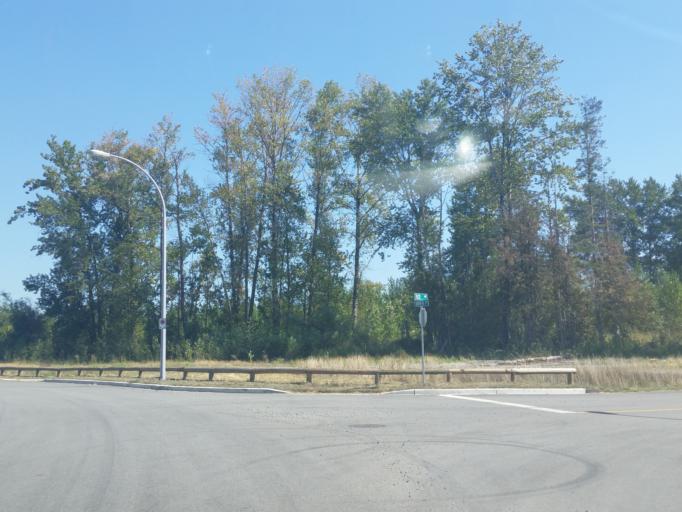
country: CA
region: British Columbia
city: Langley
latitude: 49.0973
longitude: -122.6982
